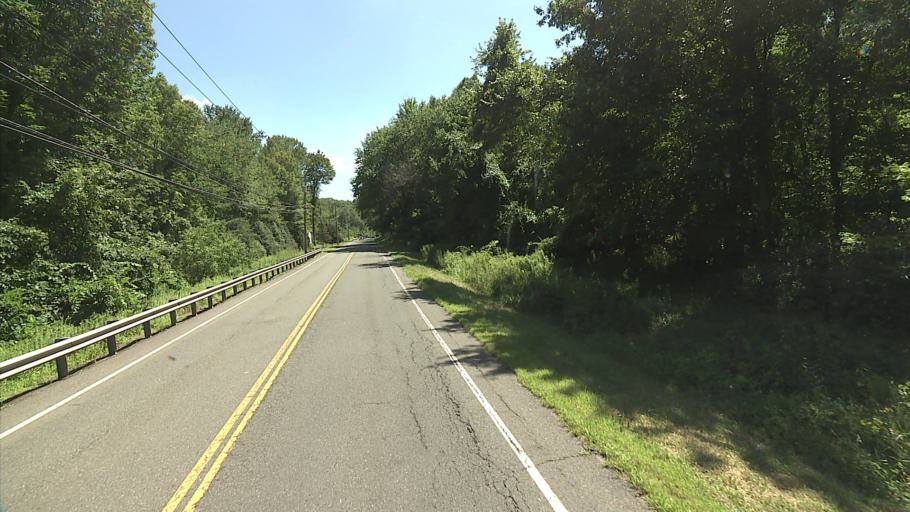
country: US
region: Massachusetts
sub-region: Hampden County
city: Southwick
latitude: 42.0143
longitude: -72.7269
